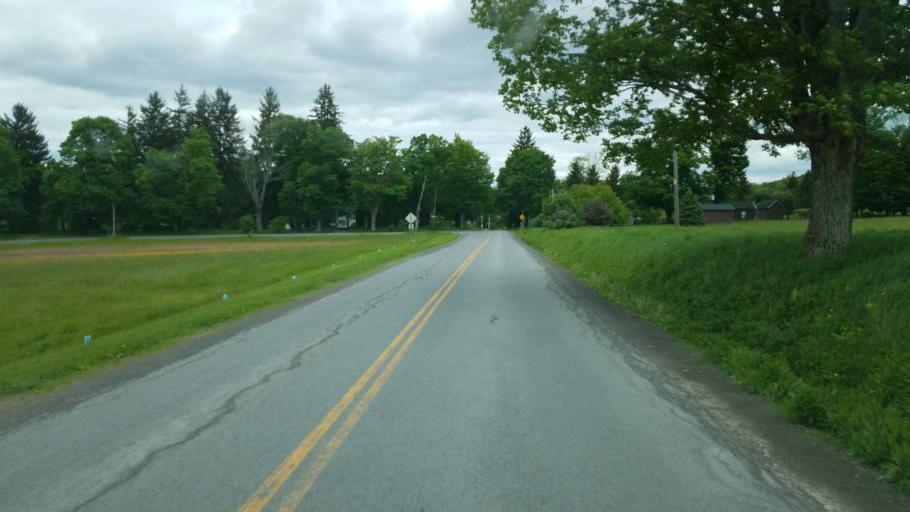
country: US
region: New York
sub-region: Otsego County
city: Richfield Springs
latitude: 42.8469
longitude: -74.9665
